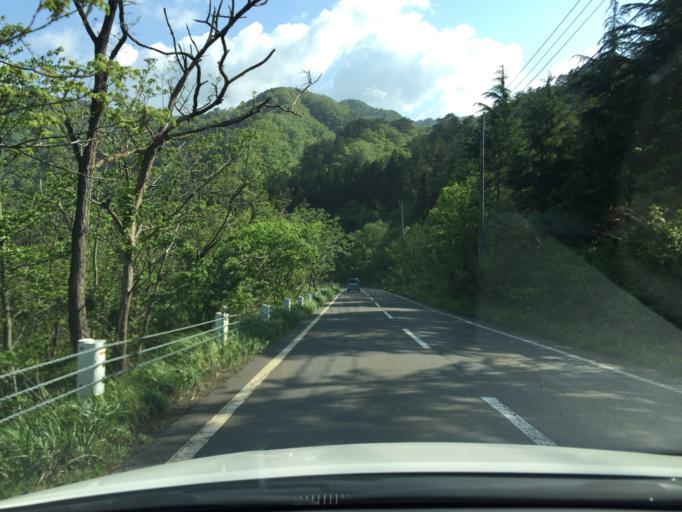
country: JP
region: Fukushima
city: Kitakata
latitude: 37.7004
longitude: 139.5693
